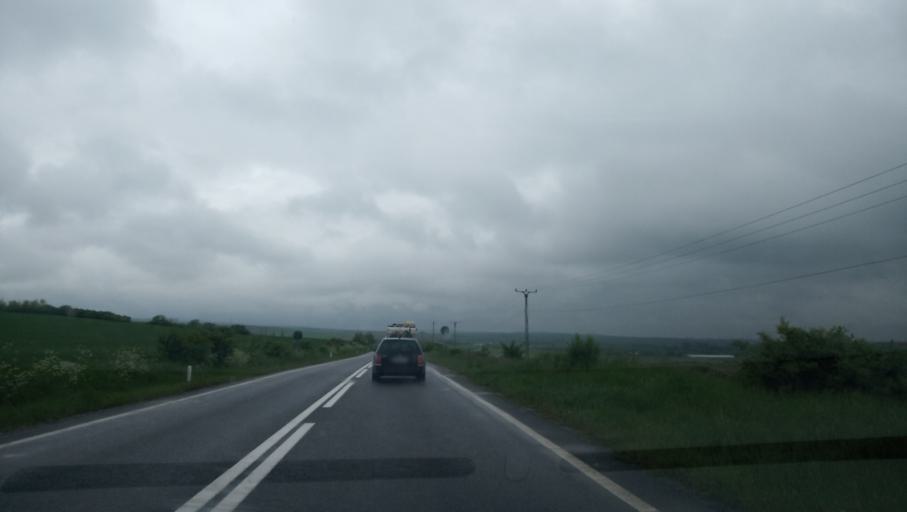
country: RO
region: Alba
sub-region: Comuna Cut
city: Cut
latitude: 45.9199
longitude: 23.6454
